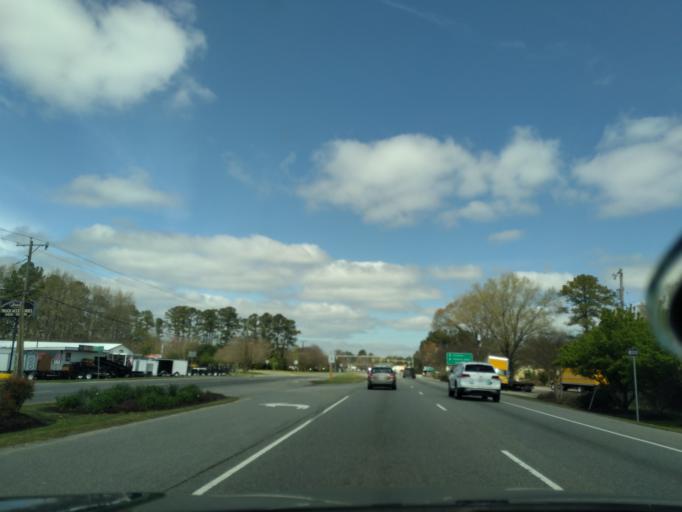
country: US
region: Virginia
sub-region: City of Poquoson
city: Poquoson
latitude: 37.1159
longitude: -76.4564
